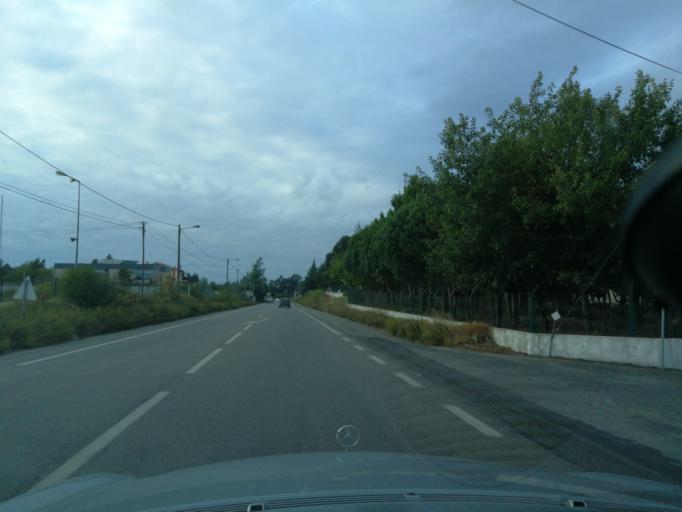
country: PT
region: Aveiro
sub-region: Agueda
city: Valongo
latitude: 40.6011
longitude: -8.4623
